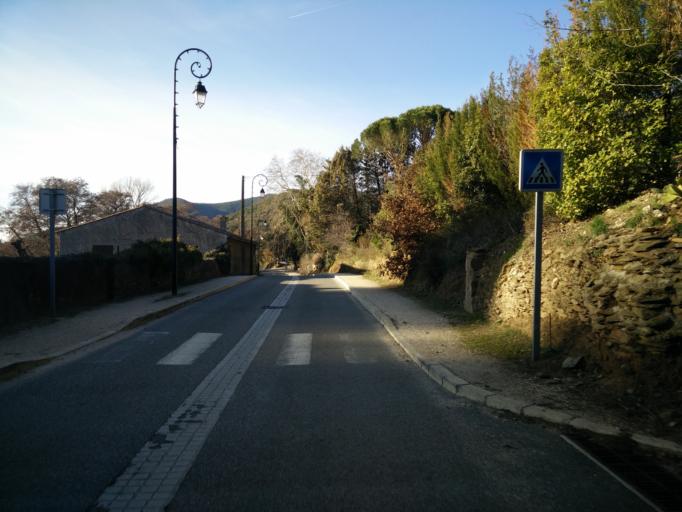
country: FR
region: Provence-Alpes-Cote d'Azur
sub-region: Departement du Var
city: Collobrieres
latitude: 43.2384
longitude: 6.3014
